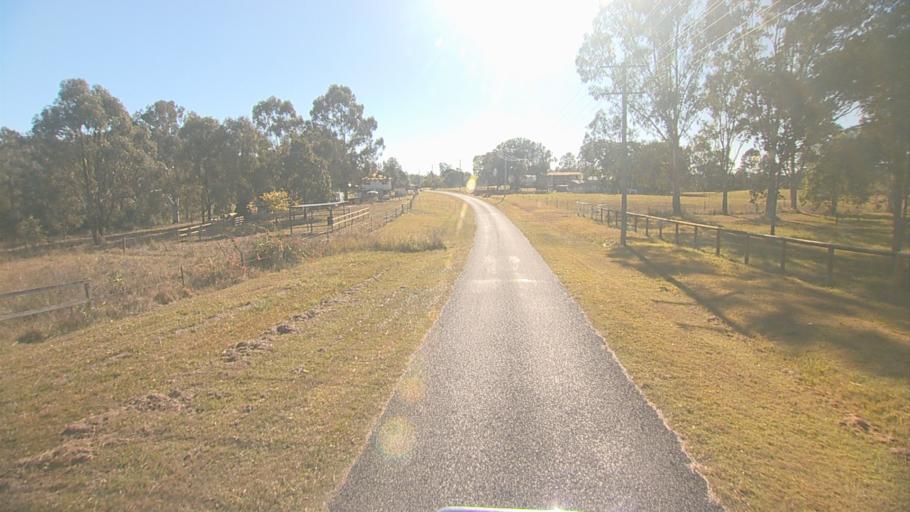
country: AU
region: Queensland
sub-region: Logan
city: Chambers Flat
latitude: -27.7590
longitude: 153.0532
